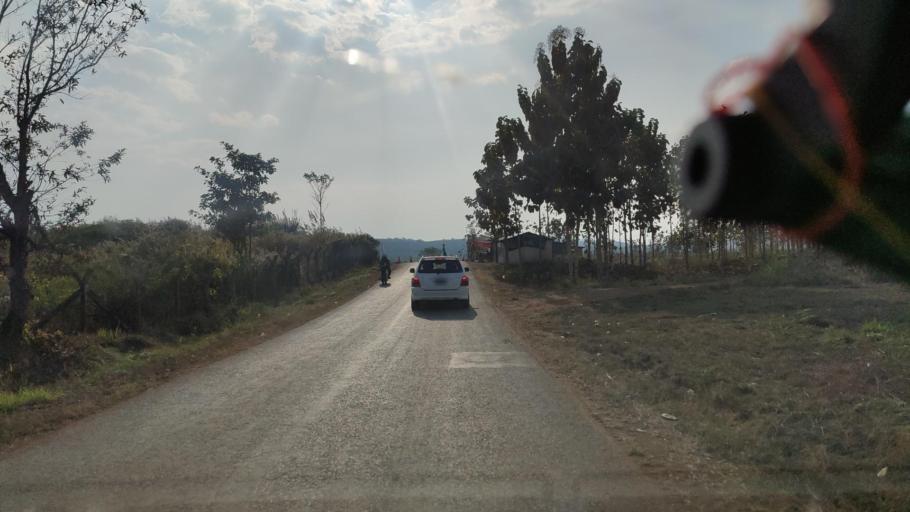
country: CN
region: Yunnan
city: Nayun
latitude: 21.8434
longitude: 99.6691
